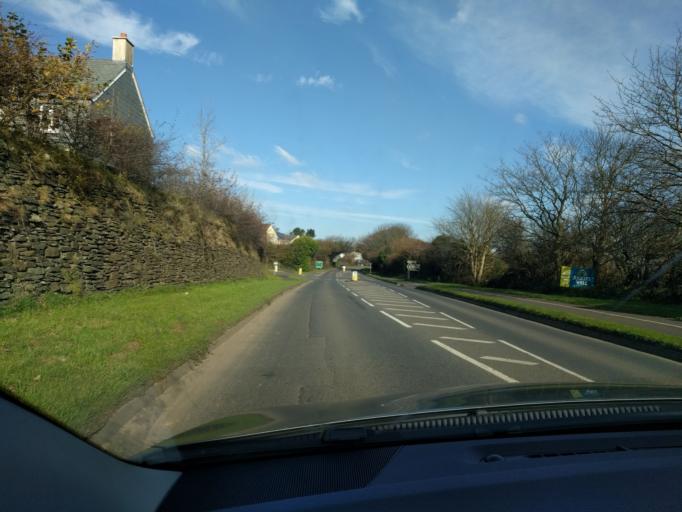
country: GB
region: England
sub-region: Cornwall
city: Camelford
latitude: 50.6131
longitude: -4.6863
